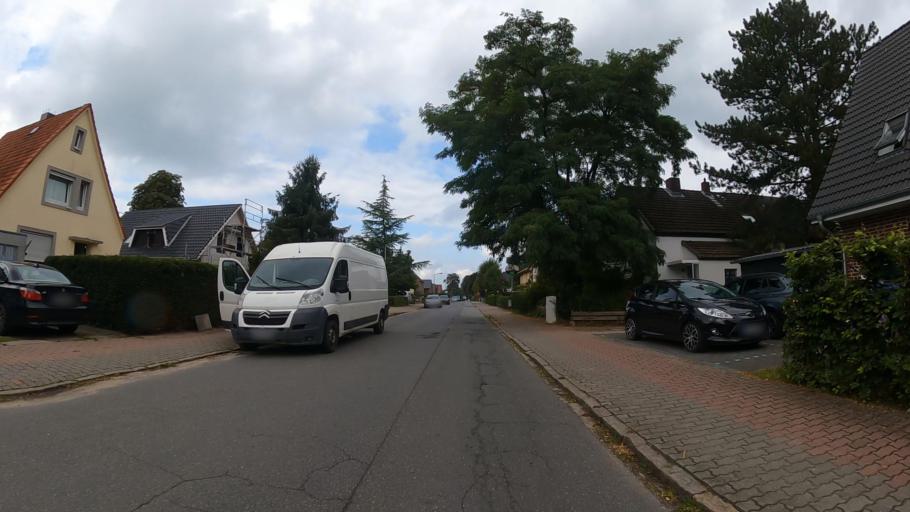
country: DE
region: Schleswig-Holstein
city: Tornesch
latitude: 53.7010
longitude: 9.7162
